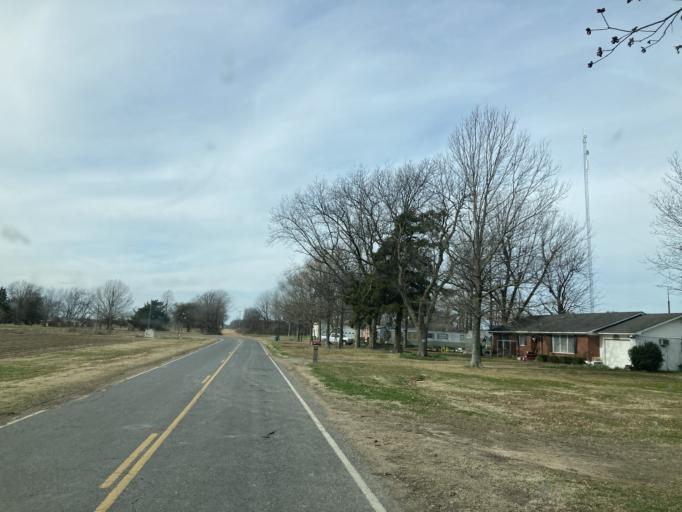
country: US
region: Mississippi
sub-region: Humphreys County
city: Belzoni
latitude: 33.1382
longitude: -90.6054
